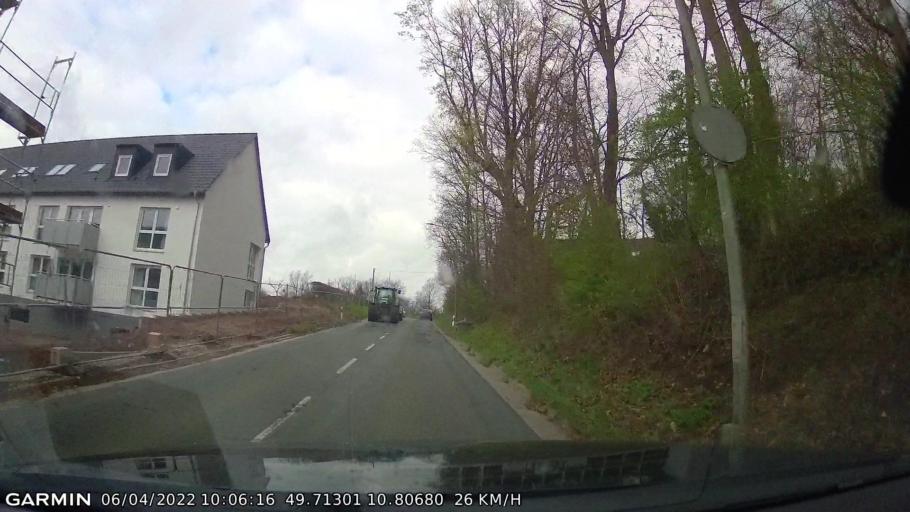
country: DE
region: Bavaria
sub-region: Regierungsbezirk Mittelfranken
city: Hochstadt an der Aisch
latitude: 49.7130
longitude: 10.8068
